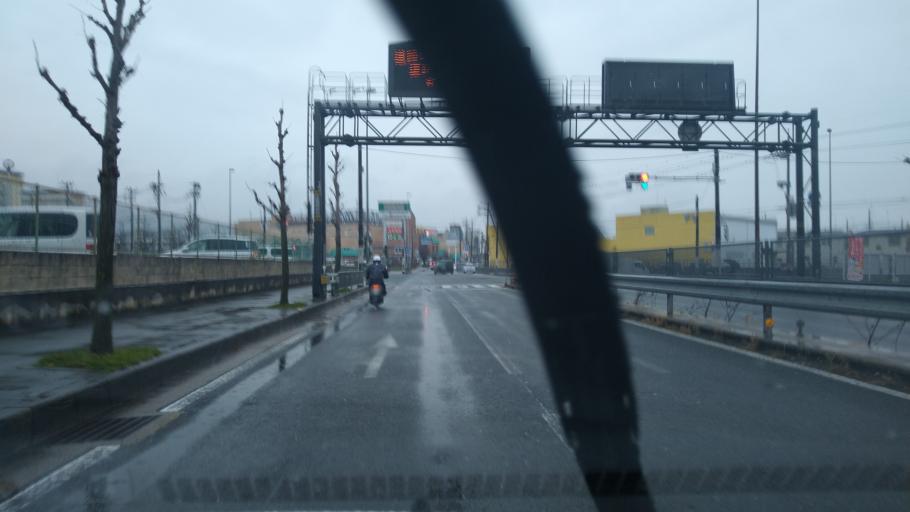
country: JP
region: Kyoto
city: Uji
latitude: 34.9178
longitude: 135.7800
